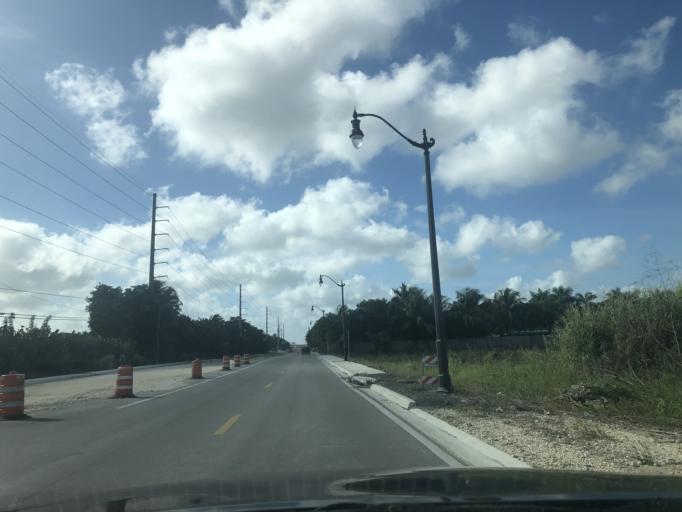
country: US
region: Florida
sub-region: Miami-Dade County
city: Homestead
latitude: 25.4628
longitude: -80.4543
